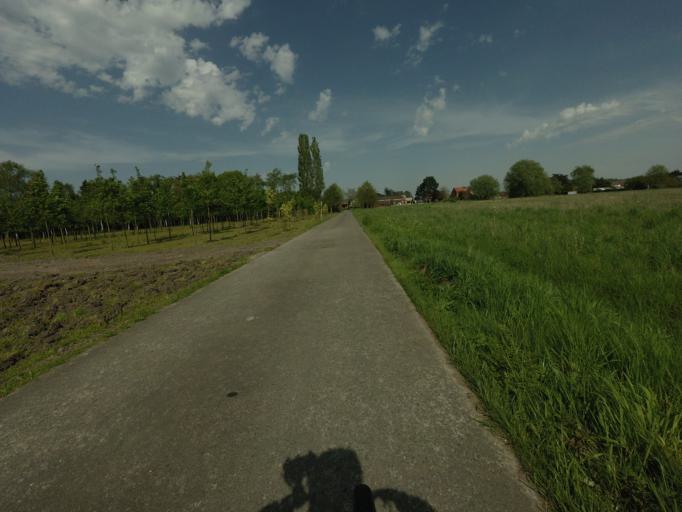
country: BE
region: Flanders
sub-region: Provincie Antwerpen
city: Putte
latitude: 51.0676
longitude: 4.6154
